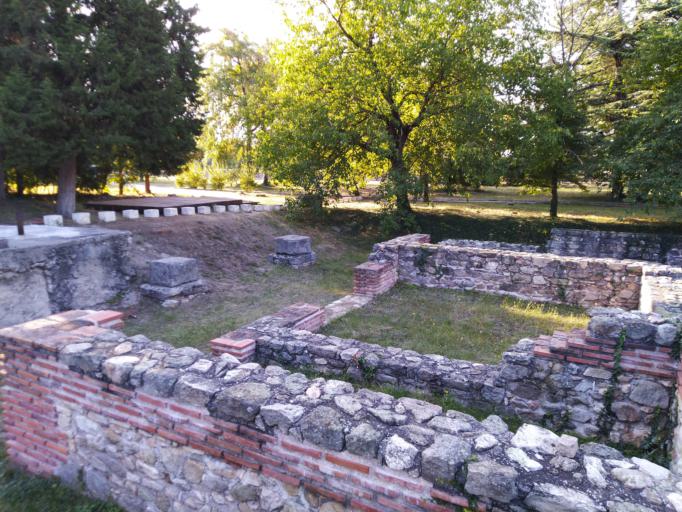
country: BG
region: Plovdiv
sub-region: Obshtina Khisarya
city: Khisarya
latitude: 42.4993
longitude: 24.7045
